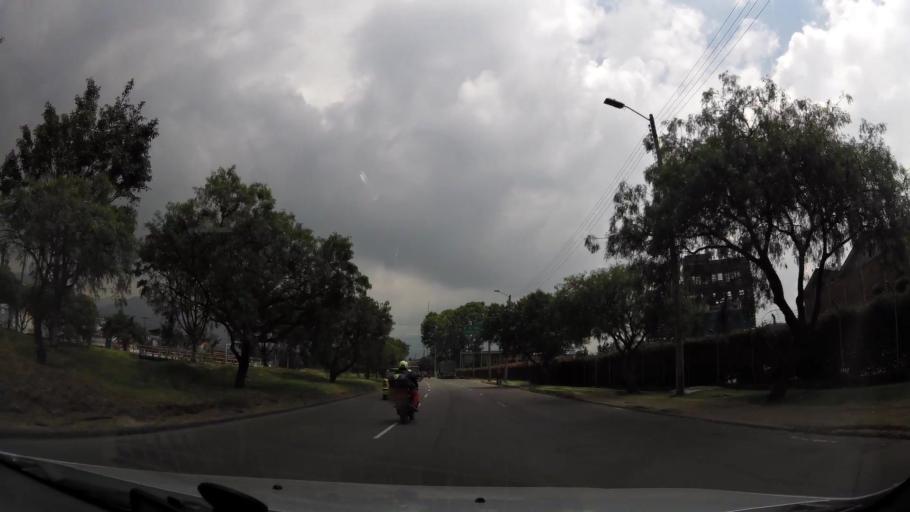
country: CO
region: Bogota D.C.
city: Bogota
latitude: 4.6125
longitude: -74.1043
